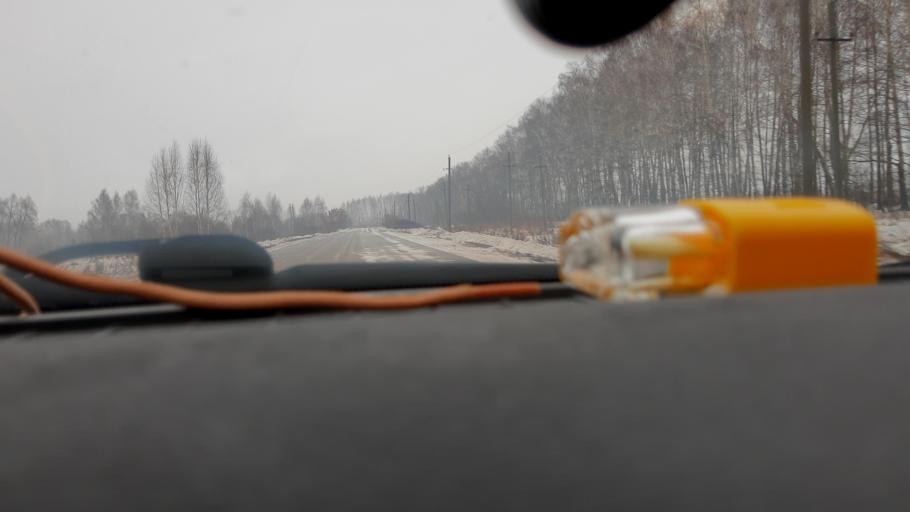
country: RU
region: Bashkortostan
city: Ulukulevo
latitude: 54.4949
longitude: 56.3929
